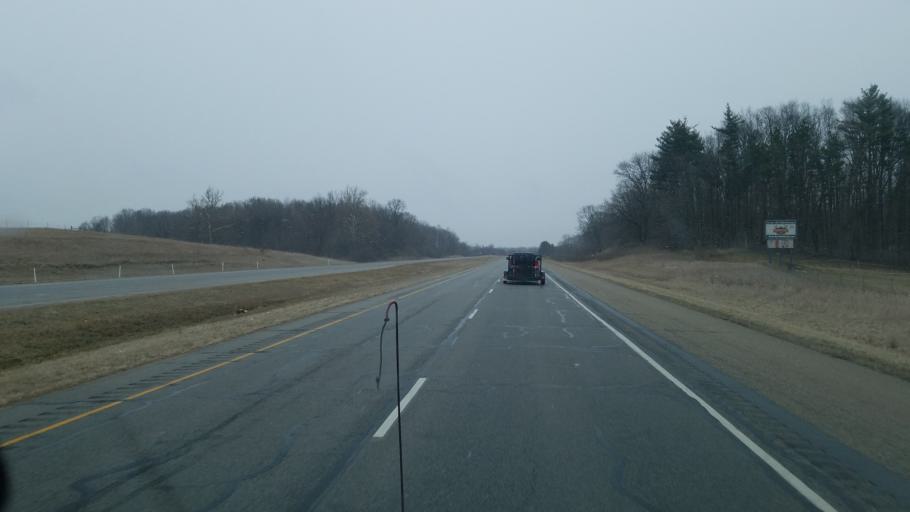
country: US
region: Indiana
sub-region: Miami County
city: Peru
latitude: 40.8016
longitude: -86.0276
